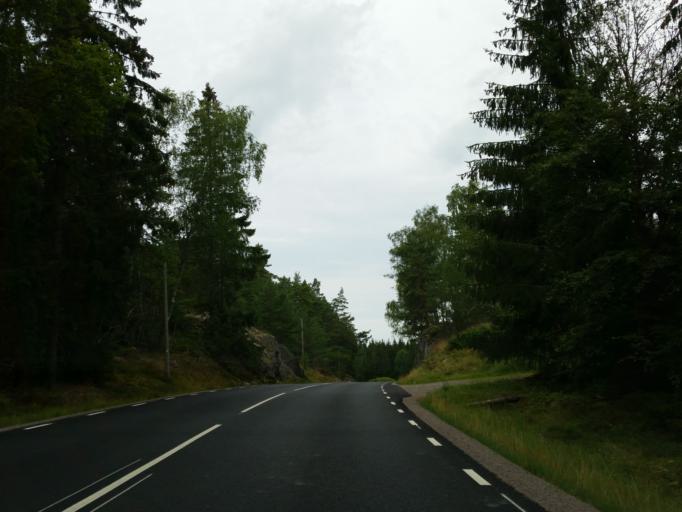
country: SE
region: Soedermanland
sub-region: Strangnas Kommun
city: Mariefred
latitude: 59.2669
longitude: 17.1602
